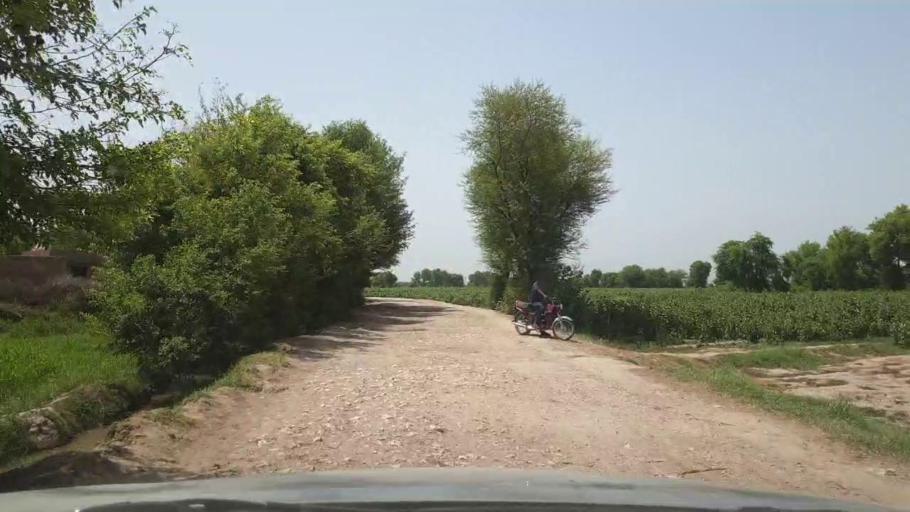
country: PK
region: Sindh
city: Pano Aqil
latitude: 27.7945
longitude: 69.2404
